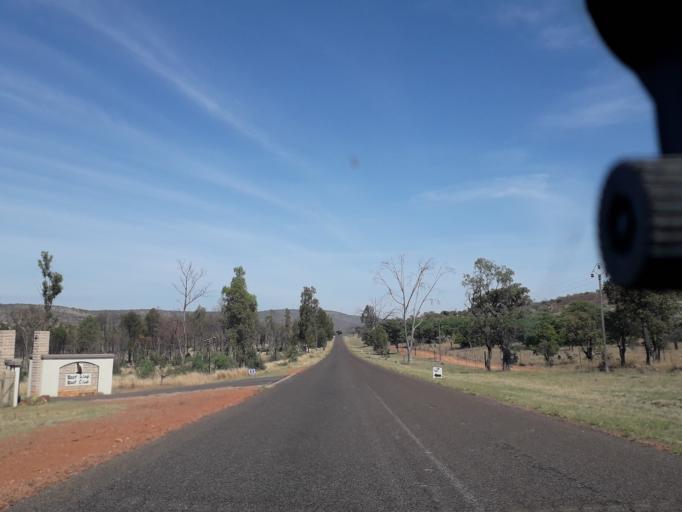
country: ZA
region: Limpopo
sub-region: Waterberg District Municipality
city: Warmbaths
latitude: -24.8401
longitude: 28.2431
